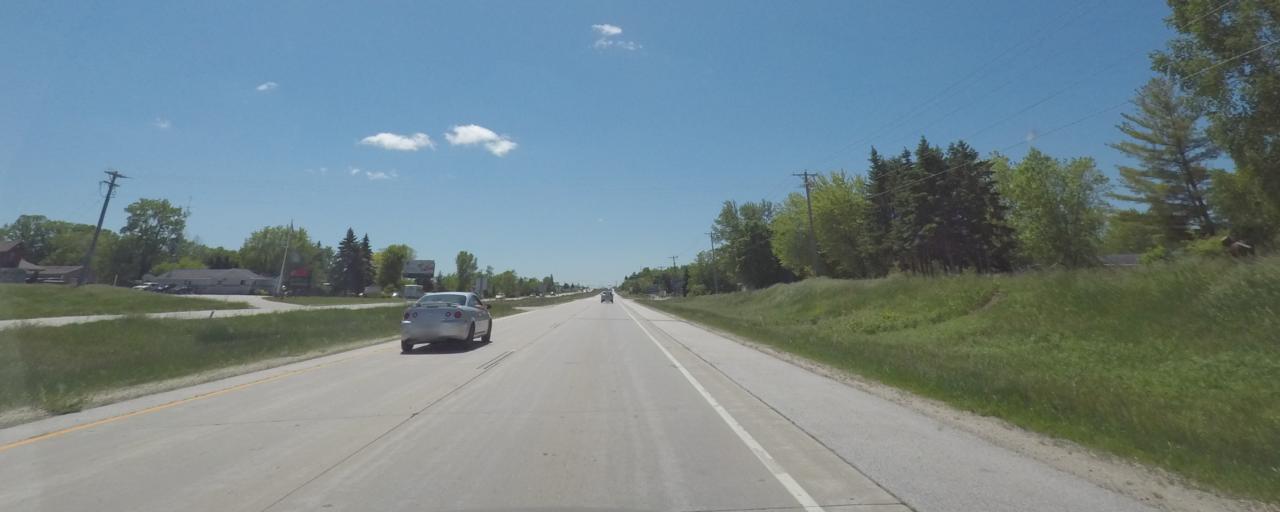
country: US
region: Wisconsin
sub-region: Sheboygan County
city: Plymouth
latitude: 43.7437
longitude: -87.9414
